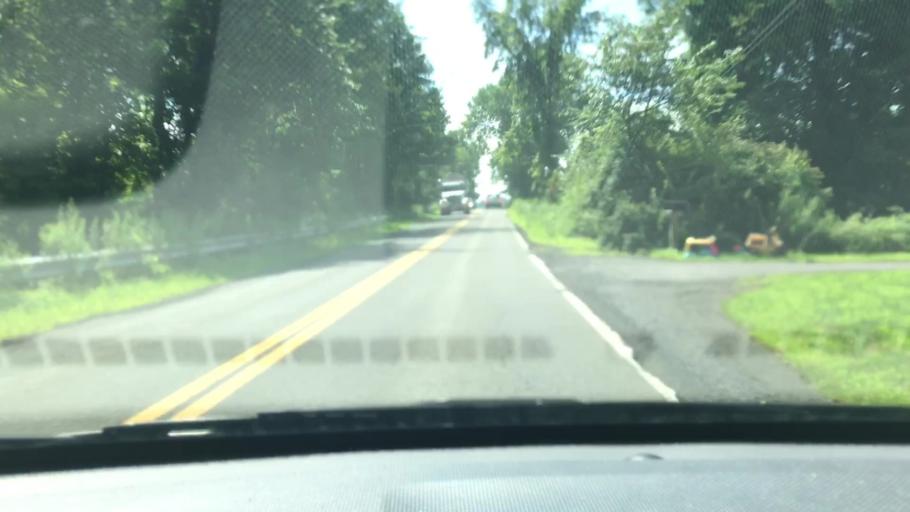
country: US
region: New York
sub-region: Ulster County
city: Stone Ridge
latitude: 41.8801
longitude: -74.1460
